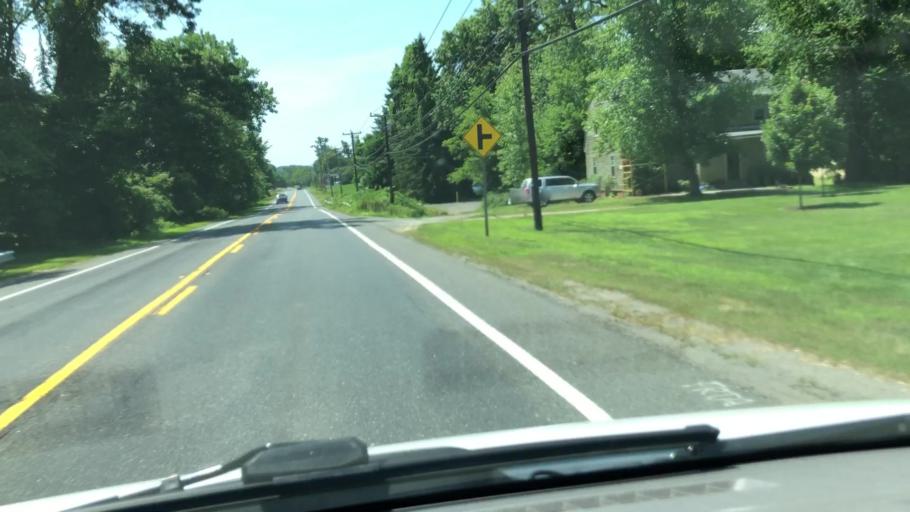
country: US
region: Massachusetts
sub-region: Franklin County
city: Greenfield
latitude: 42.5428
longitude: -72.6019
